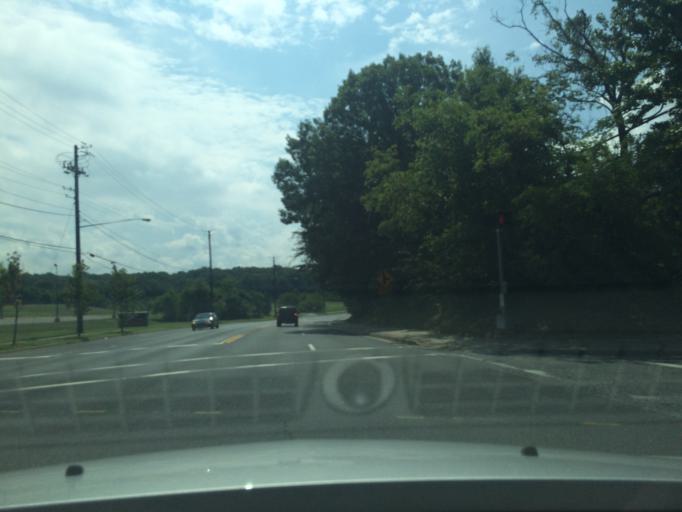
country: US
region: Maryland
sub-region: Prince George's County
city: Coral Hills
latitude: 38.8700
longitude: -76.9203
